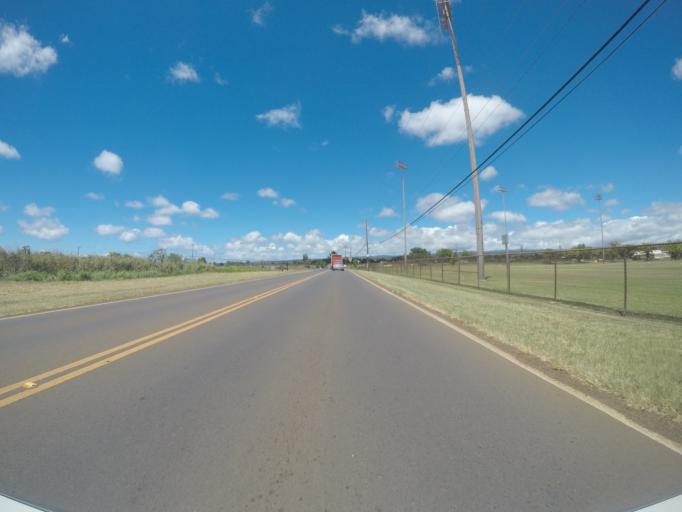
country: US
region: Hawaii
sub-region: Honolulu County
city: Waialua
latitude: 21.5769
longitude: -158.1237
